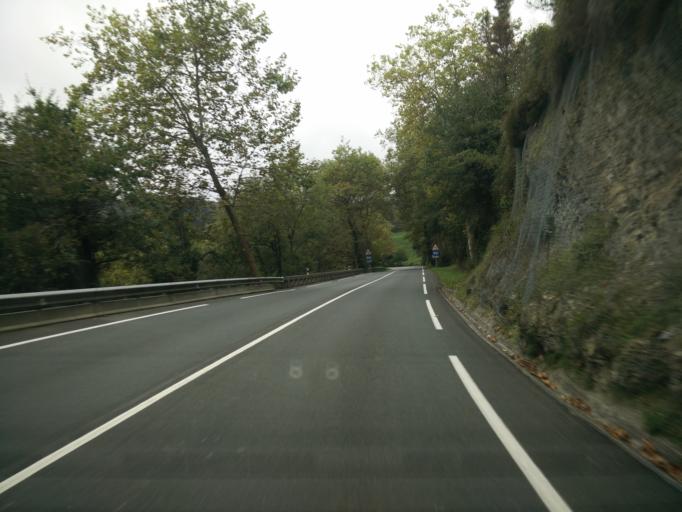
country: ES
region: Basque Country
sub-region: Provincia de Guipuzcoa
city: Zumaia
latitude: 43.2813
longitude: -2.2948
